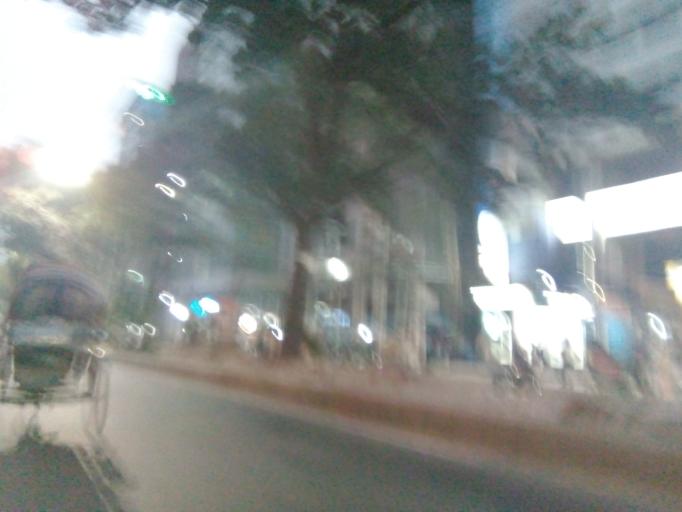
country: BD
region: Dhaka
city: Paltan
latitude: 23.7353
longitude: 90.4103
